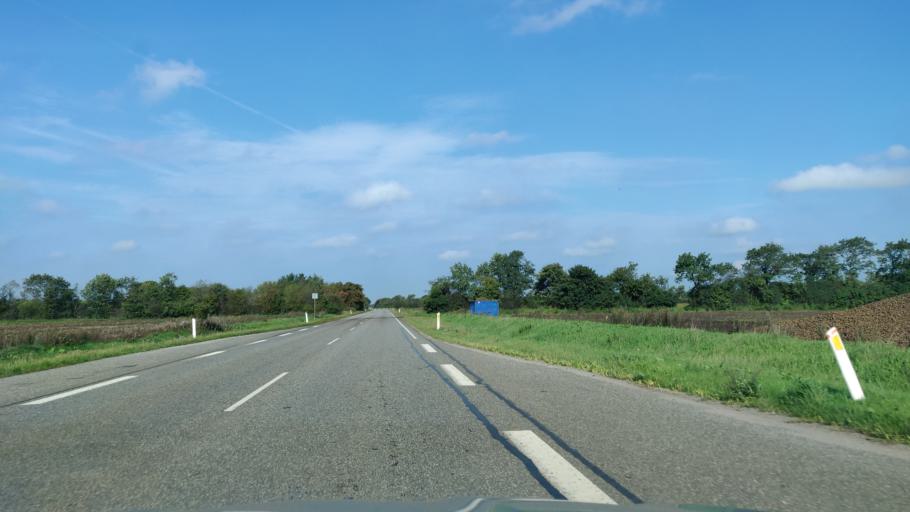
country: DK
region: Central Jutland
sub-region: Herning Kommune
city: Sunds
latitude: 56.2535
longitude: 9.0503
